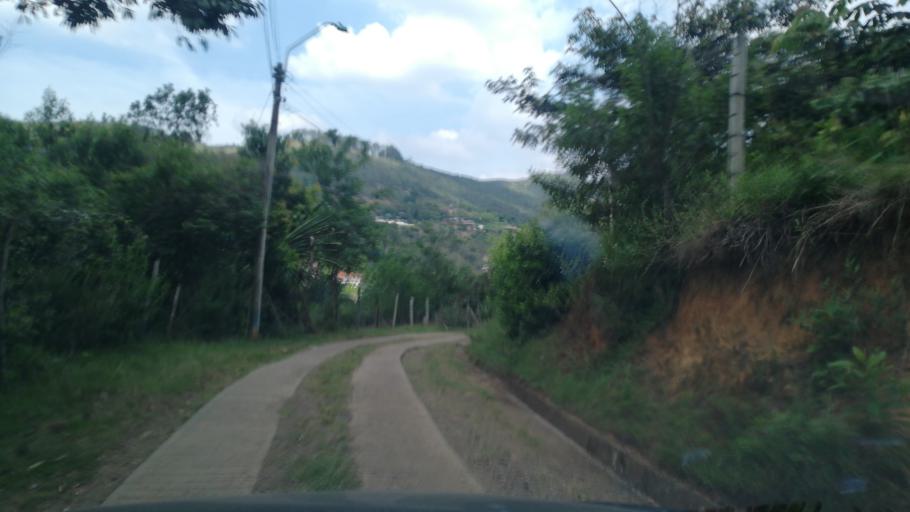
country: CO
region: Valle del Cauca
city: Cali
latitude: 3.4827
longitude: -76.5556
